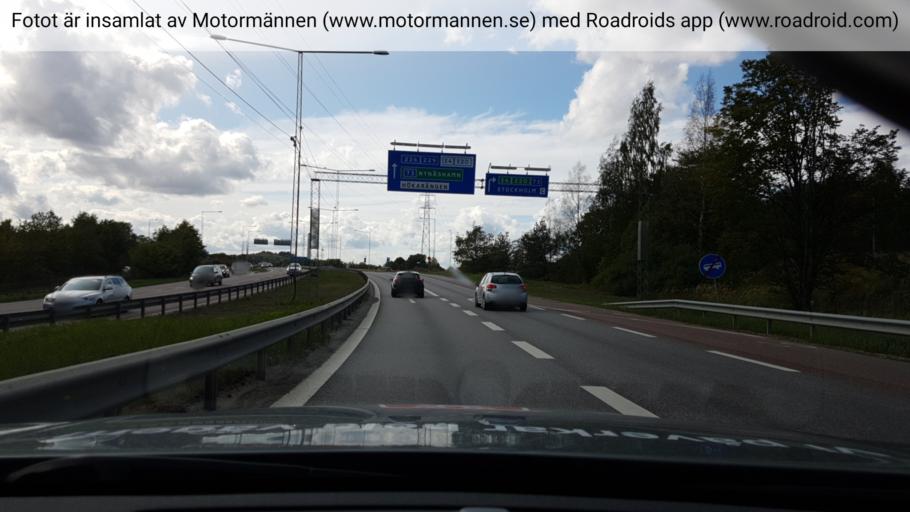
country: SE
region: Stockholm
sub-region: Stockholms Kommun
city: Arsta
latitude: 59.2618
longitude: 18.1049
